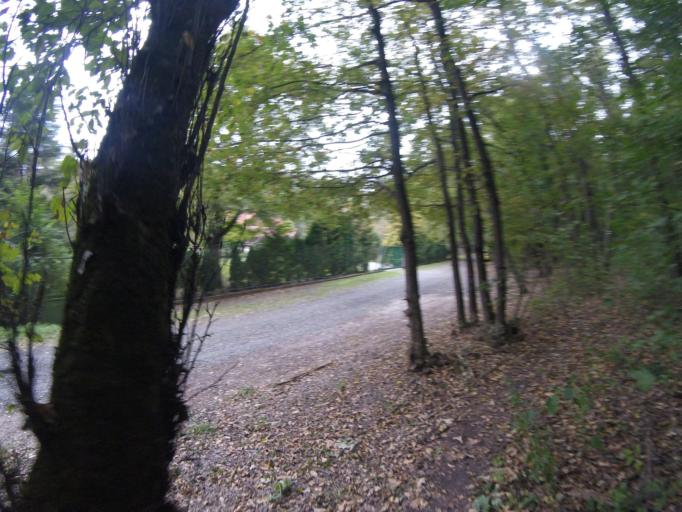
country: HU
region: Pest
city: Szob
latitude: 47.8165
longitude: 18.9161
